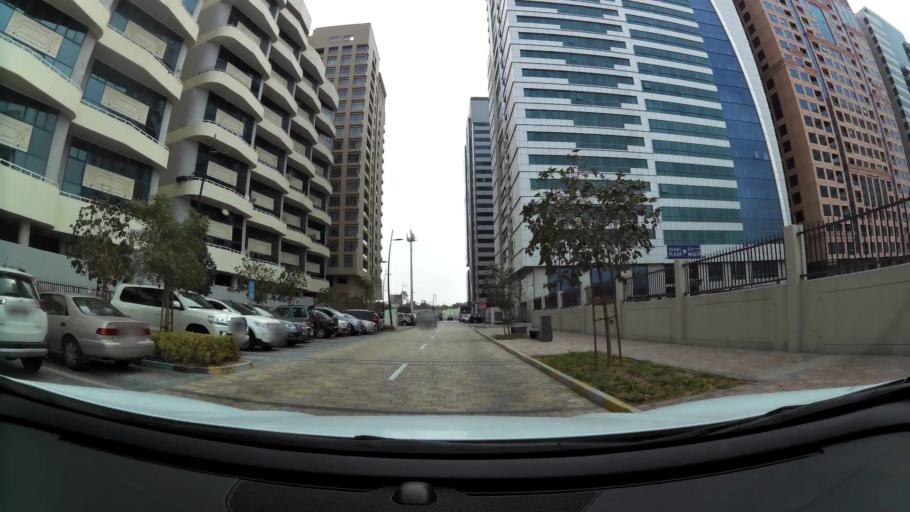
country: AE
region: Abu Dhabi
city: Abu Dhabi
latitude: 24.4699
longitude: 54.3398
